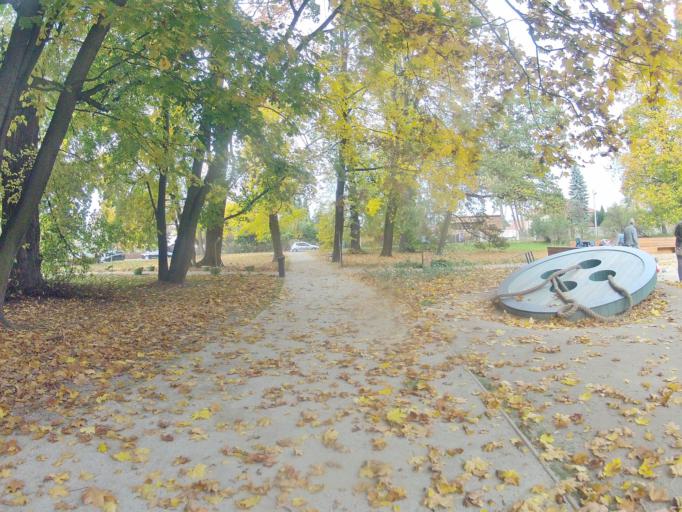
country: PL
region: Lesser Poland Voivodeship
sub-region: Powiat krakowski
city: Rzaska
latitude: 50.0660
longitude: 19.8726
